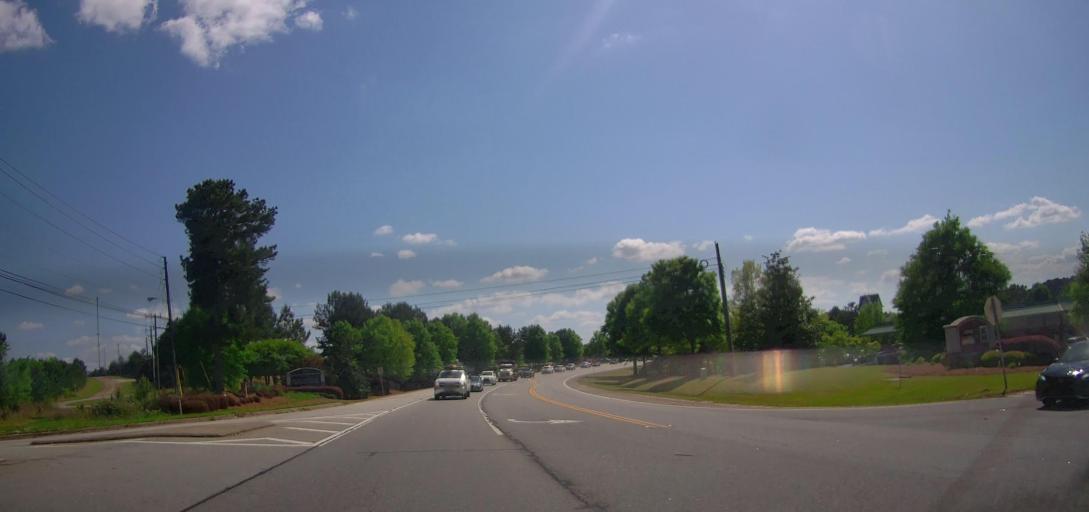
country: US
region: Georgia
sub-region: Putnam County
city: Jefferson
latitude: 33.4606
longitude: -83.2421
